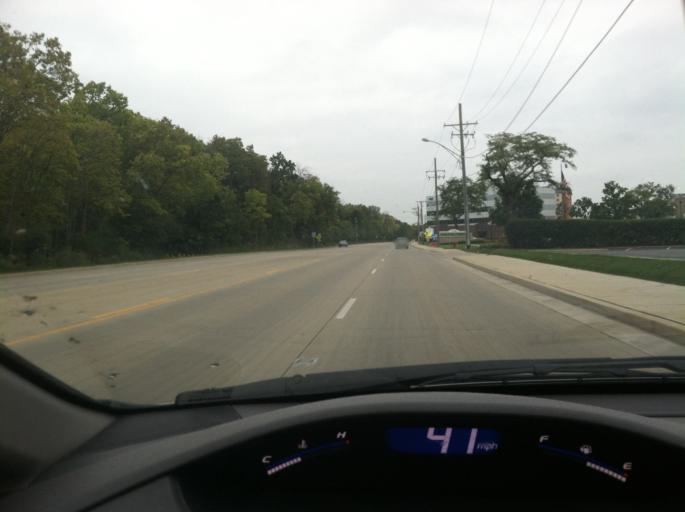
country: US
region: Illinois
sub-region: Cook County
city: Rosemont
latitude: 42.0100
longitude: -87.8714
